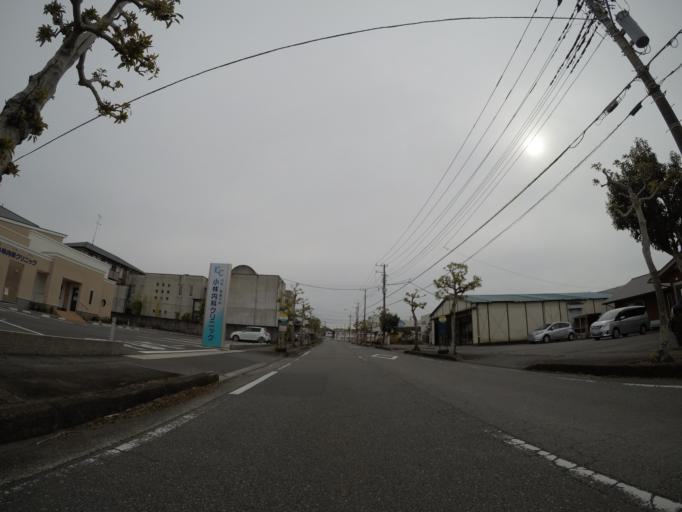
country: JP
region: Shizuoka
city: Fujinomiya
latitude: 35.2520
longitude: 138.6363
